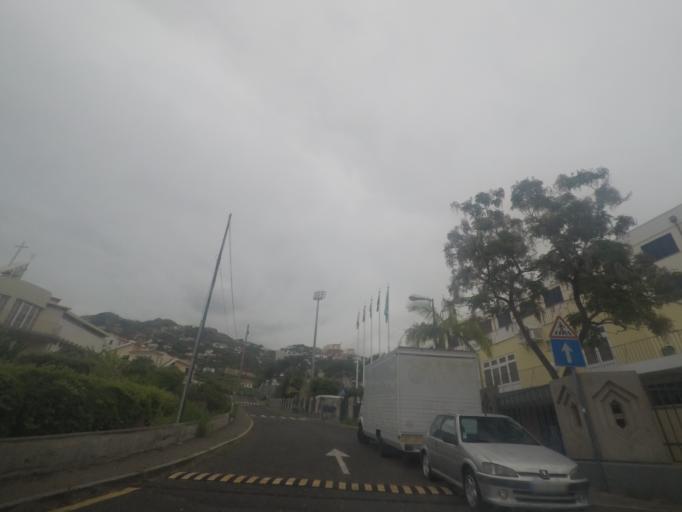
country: PT
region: Madeira
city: Camara de Lobos
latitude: 32.6533
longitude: -16.9819
